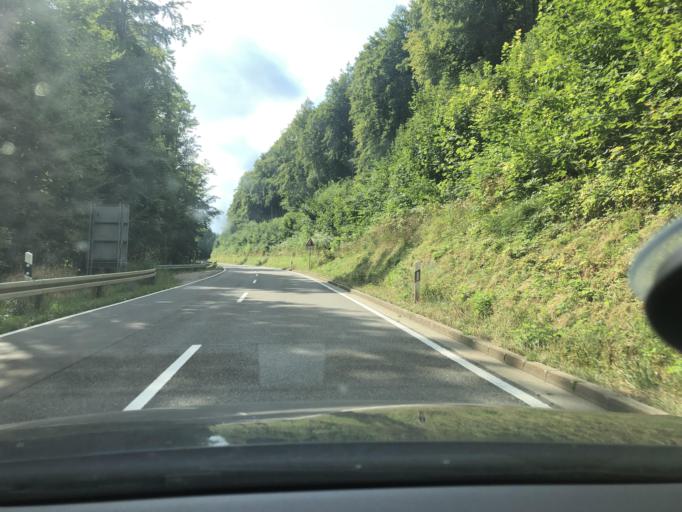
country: DE
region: Baden-Wuerttemberg
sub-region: Tuebingen Region
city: Pfullingen
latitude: 48.4303
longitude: 9.2032
